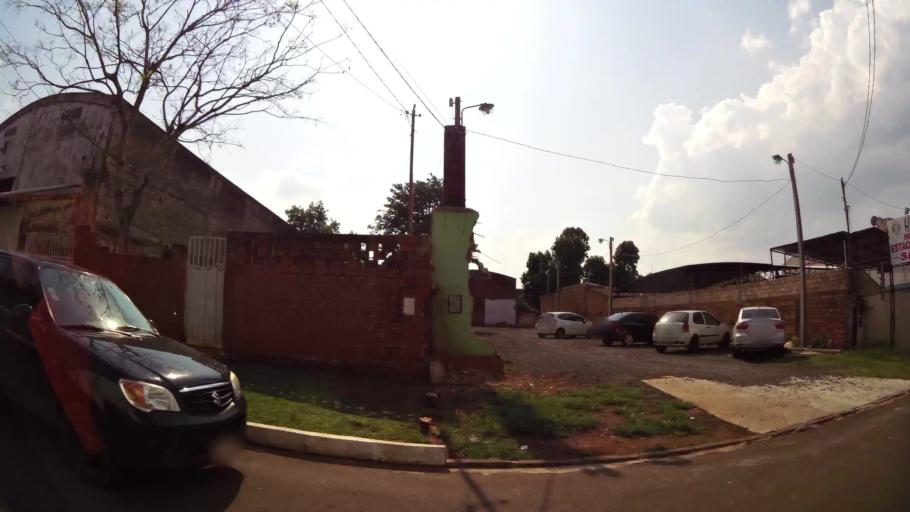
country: PY
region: Alto Parana
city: Ciudad del Este
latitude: -25.5034
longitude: -54.6334
